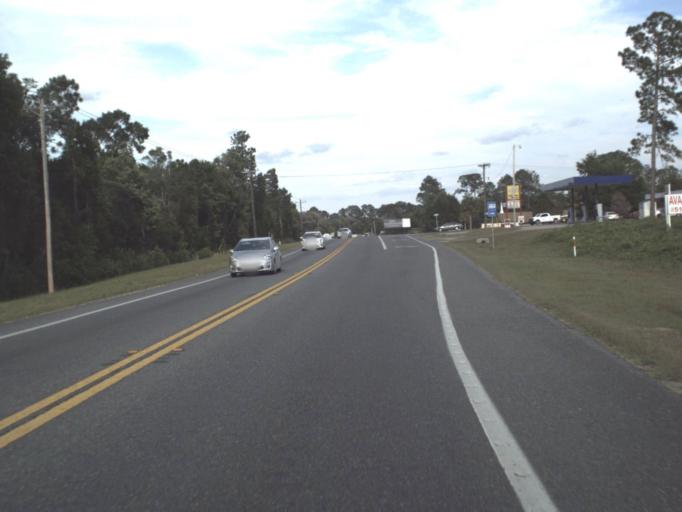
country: US
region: Florida
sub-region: Marion County
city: Silver Springs Shores
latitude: 29.1719
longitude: -81.8518
